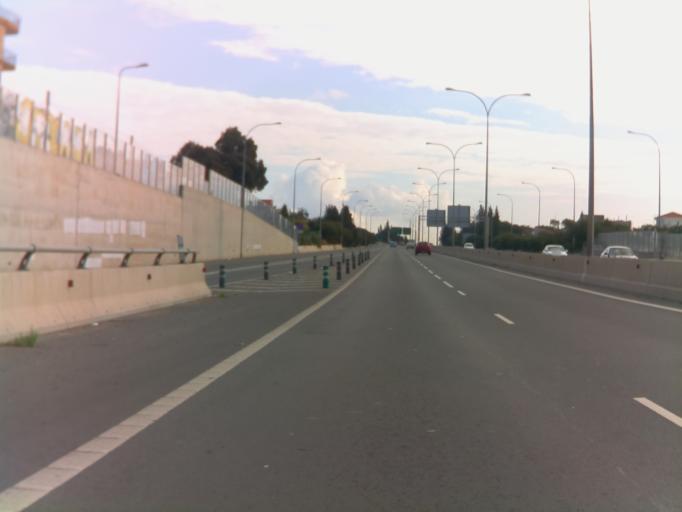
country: CY
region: Limassol
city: Limassol
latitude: 34.7049
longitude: 33.0312
